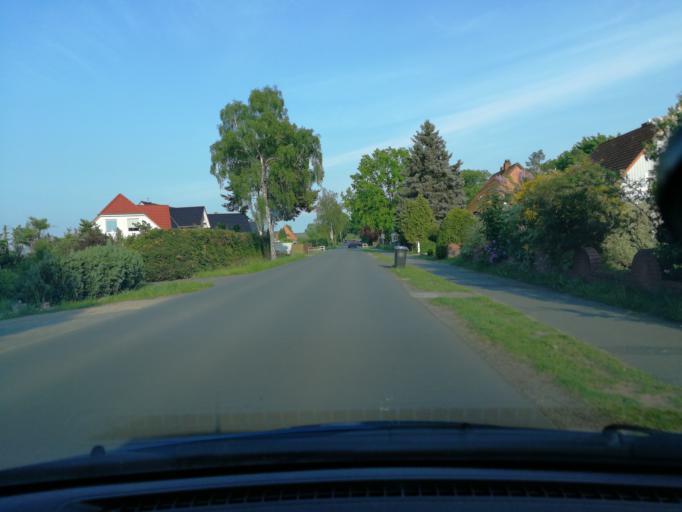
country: DE
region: Lower Saxony
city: Scharnebeck
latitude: 53.2932
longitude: 10.5155
